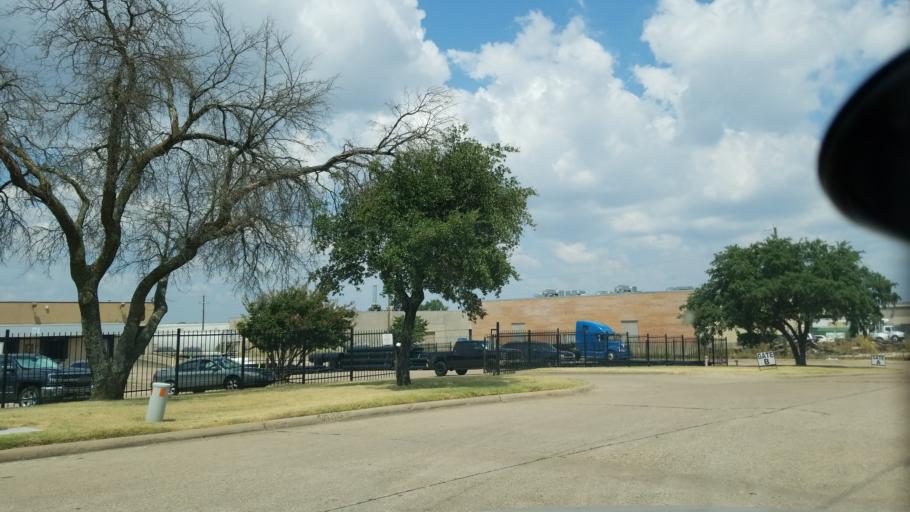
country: US
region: Texas
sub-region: Dallas County
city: Duncanville
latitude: 32.6857
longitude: -96.8985
